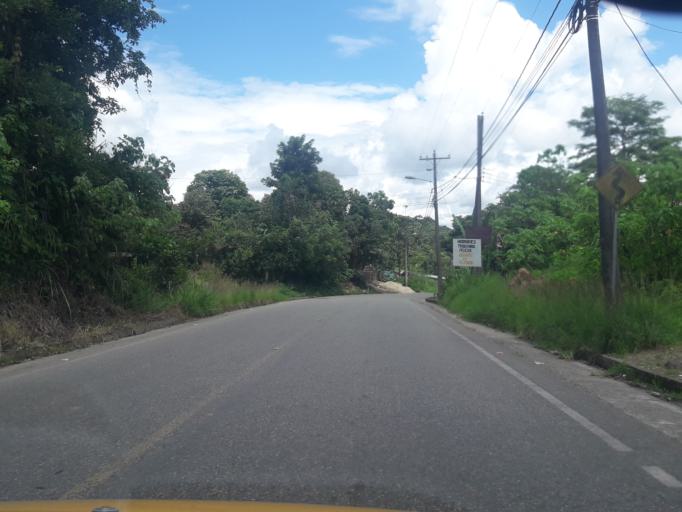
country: EC
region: Napo
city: Tena
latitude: -1.0077
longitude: -77.8203
